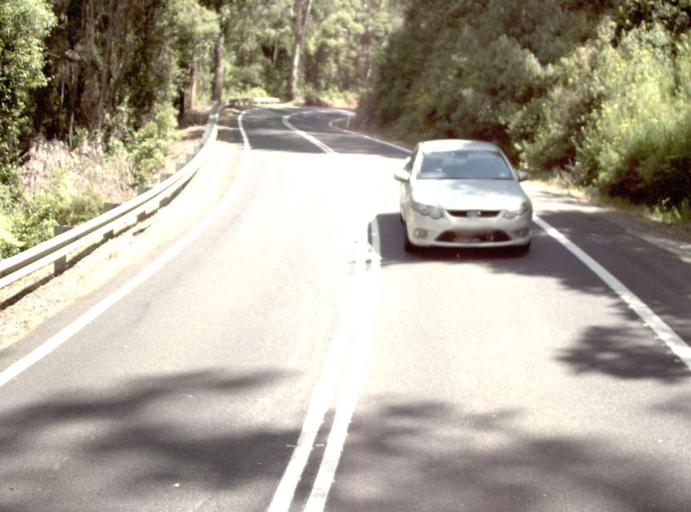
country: AU
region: New South Wales
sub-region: Bombala
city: Bombala
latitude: -37.5562
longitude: 149.3541
